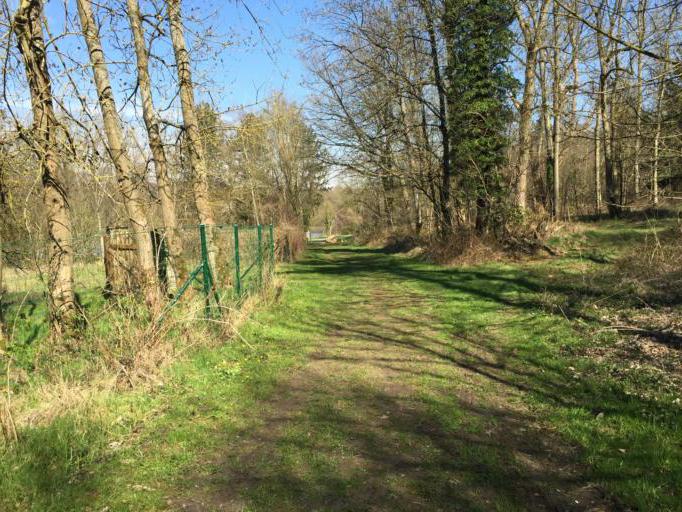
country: FR
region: Ile-de-France
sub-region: Departement des Yvelines
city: Jouy-en-Josas
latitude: 48.7585
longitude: 2.1588
